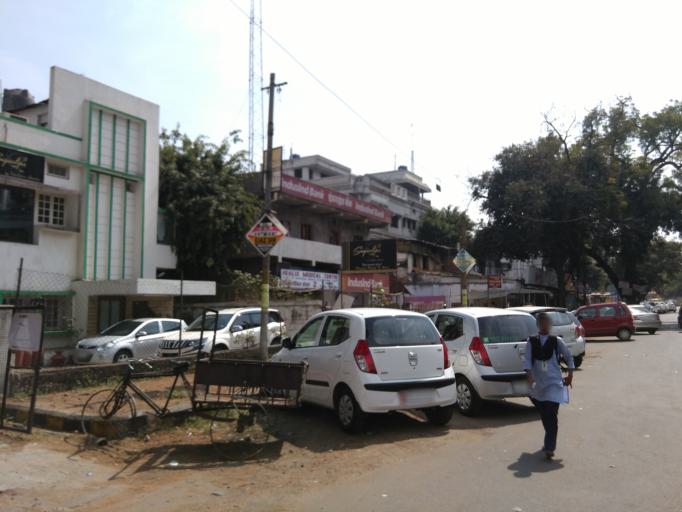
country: IN
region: Maharashtra
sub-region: Nagpur Division
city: Nagpur
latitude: 21.1687
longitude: 79.0793
